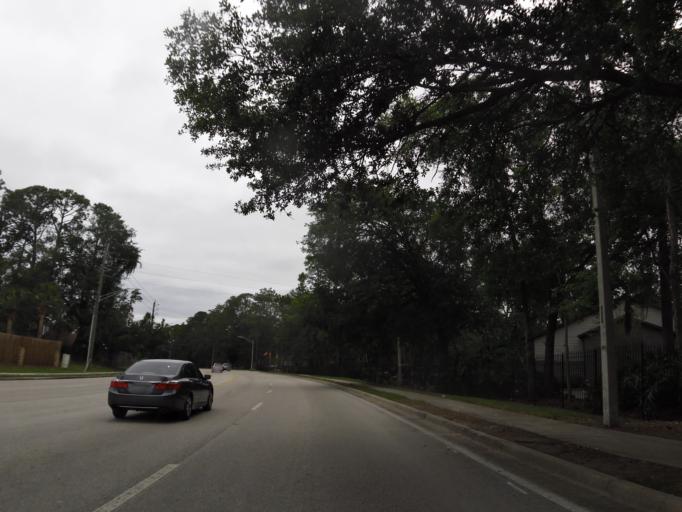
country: US
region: Florida
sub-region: Saint Johns County
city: Fruit Cove
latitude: 30.1896
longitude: -81.6080
